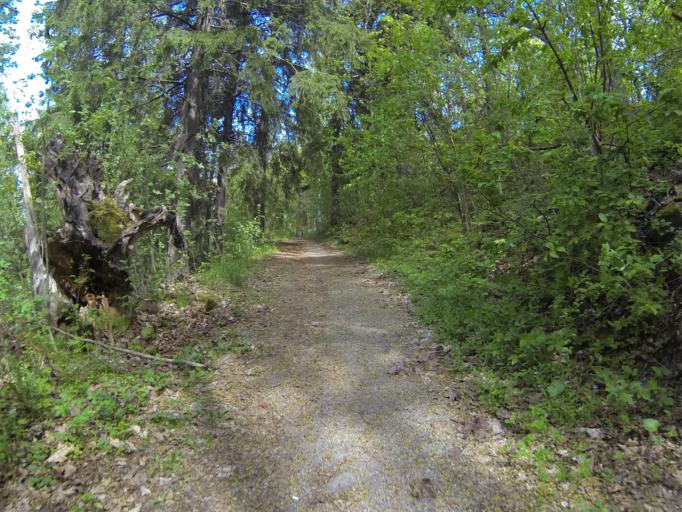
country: FI
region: Varsinais-Suomi
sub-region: Salo
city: Salo
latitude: 60.3758
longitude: 23.1262
